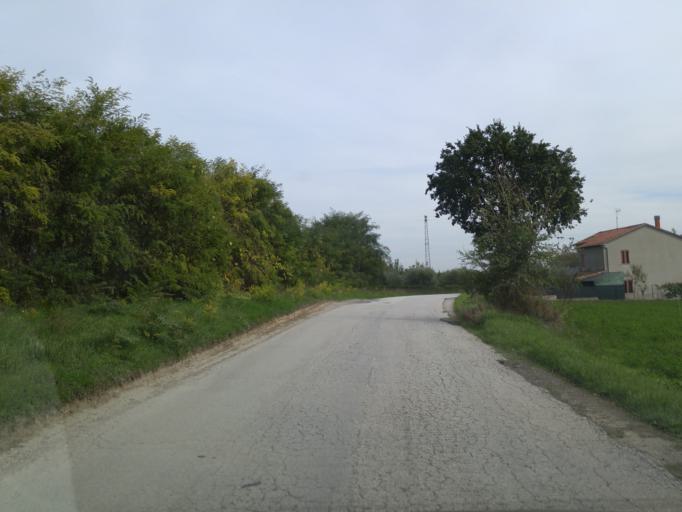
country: IT
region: The Marches
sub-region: Provincia di Pesaro e Urbino
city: Lucrezia
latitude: 43.7643
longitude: 12.9451
